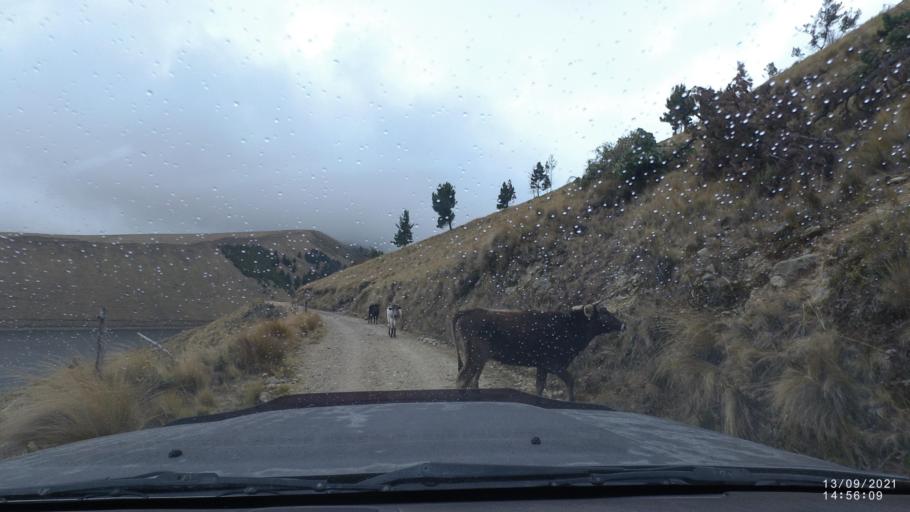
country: BO
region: Cochabamba
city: Colomi
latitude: -17.3379
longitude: -65.7910
